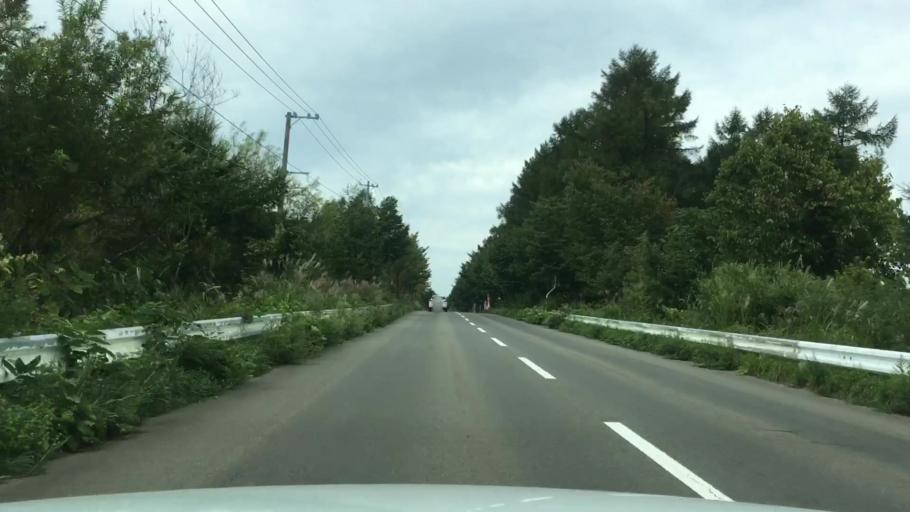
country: JP
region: Aomori
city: Shimokizukuri
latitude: 40.7106
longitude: 140.3329
